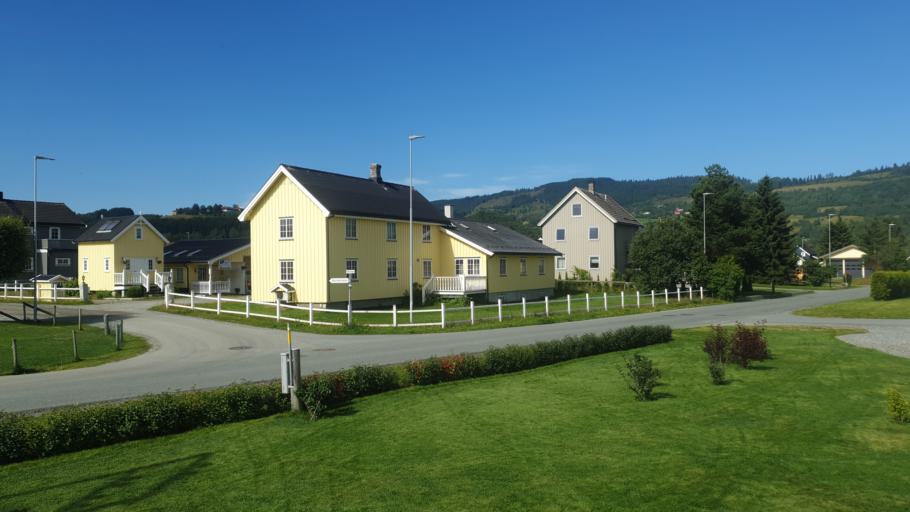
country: NO
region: Sor-Trondelag
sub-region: Orkdal
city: Orkanger
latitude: 63.2748
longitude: 9.8228
